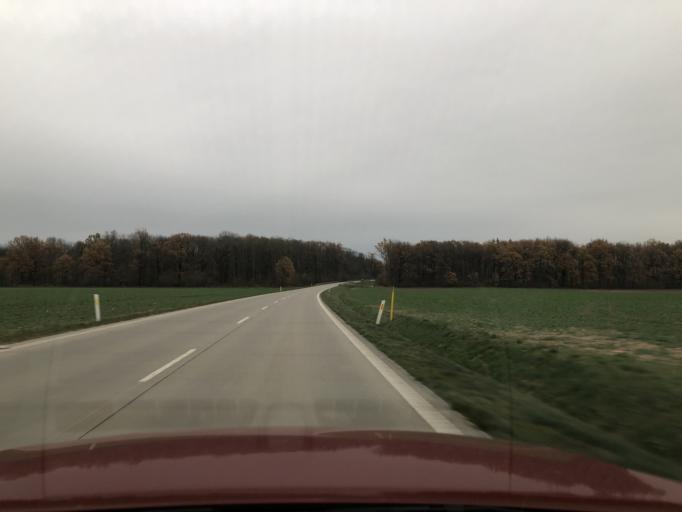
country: PL
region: Lower Silesian Voivodeship
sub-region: Powiat swidnicki
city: Zarow
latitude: 50.9421
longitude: 16.4745
